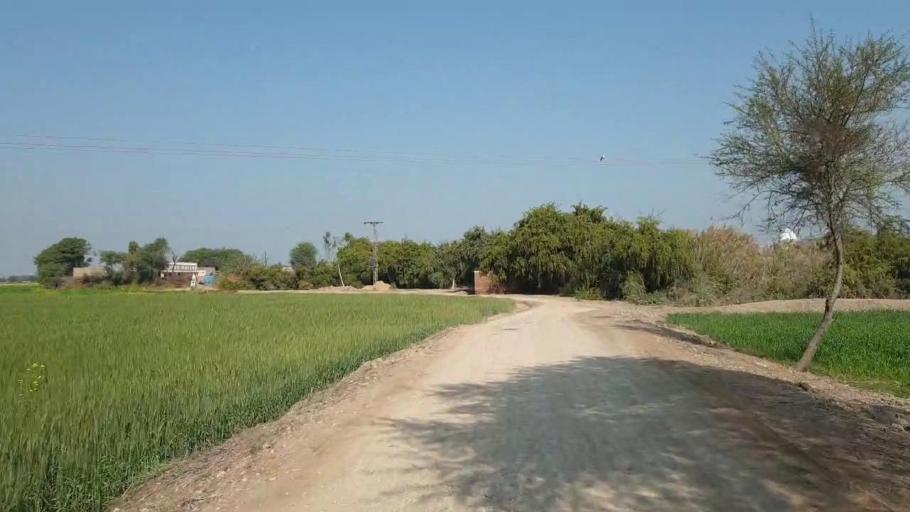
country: PK
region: Sindh
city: Hala
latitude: 25.9307
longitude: 68.4046
